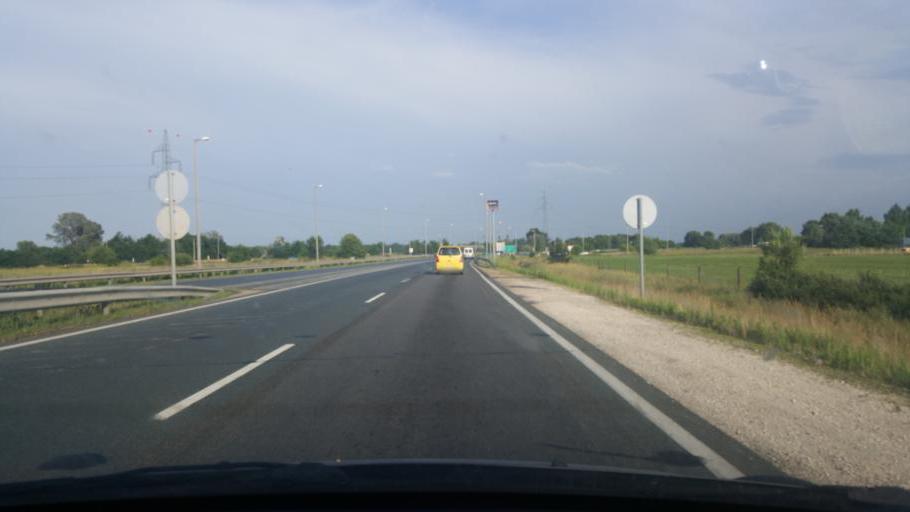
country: HU
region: Pest
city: Ullo
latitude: 47.3959
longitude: 19.3643
